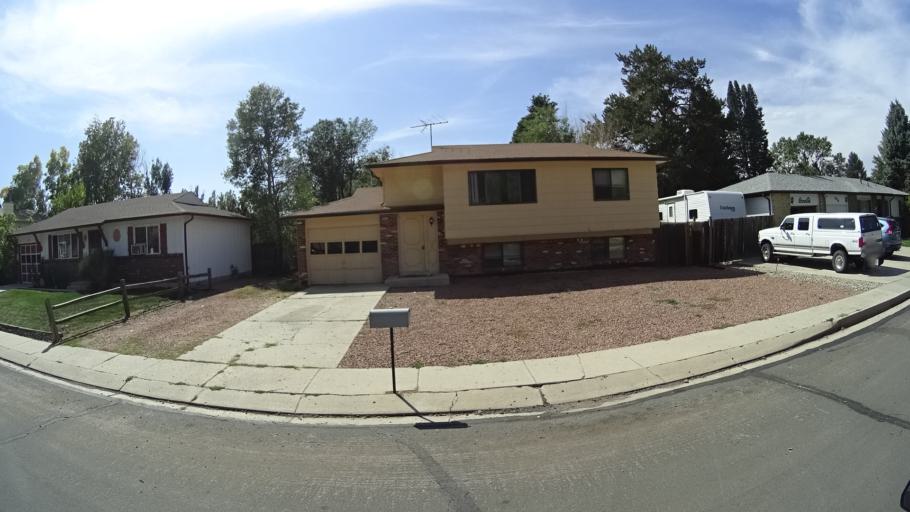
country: US
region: Colorado
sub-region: El Paso County
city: Cimarron Hills
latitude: 38.9000
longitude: -104.7543
